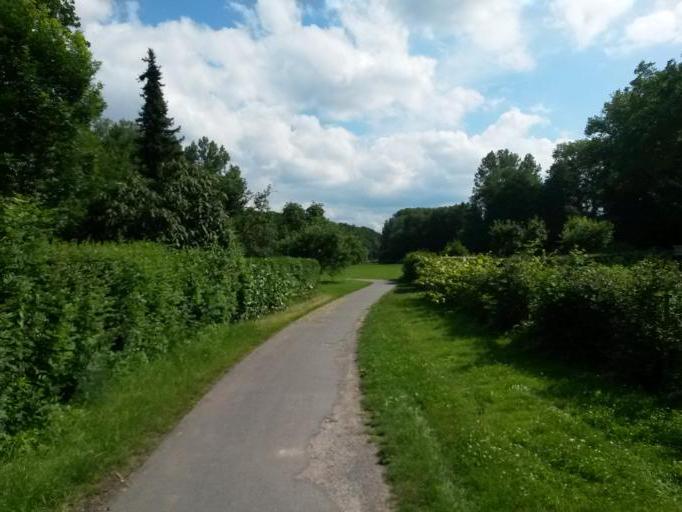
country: DE
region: Baden-Wuerttemberg
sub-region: Karlsruhe Region
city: Konigsbach-Stein
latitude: 48.9396
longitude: 8.5758
